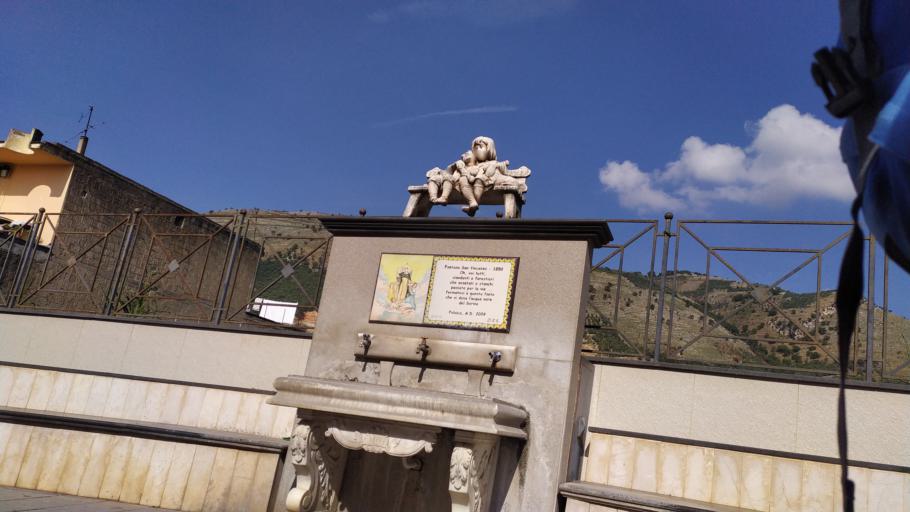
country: IT
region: Campania
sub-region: Provincia di Caserta
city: San Felice A Cancello
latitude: 40.9831
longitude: 14.4612
